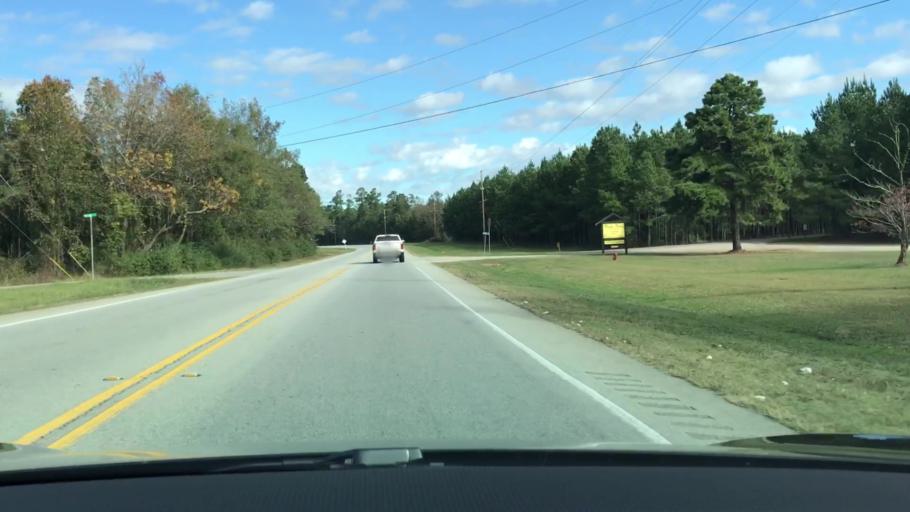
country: US
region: Georgia
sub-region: Jefferson County
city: Louisville
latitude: 33.0525
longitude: -82.4065
